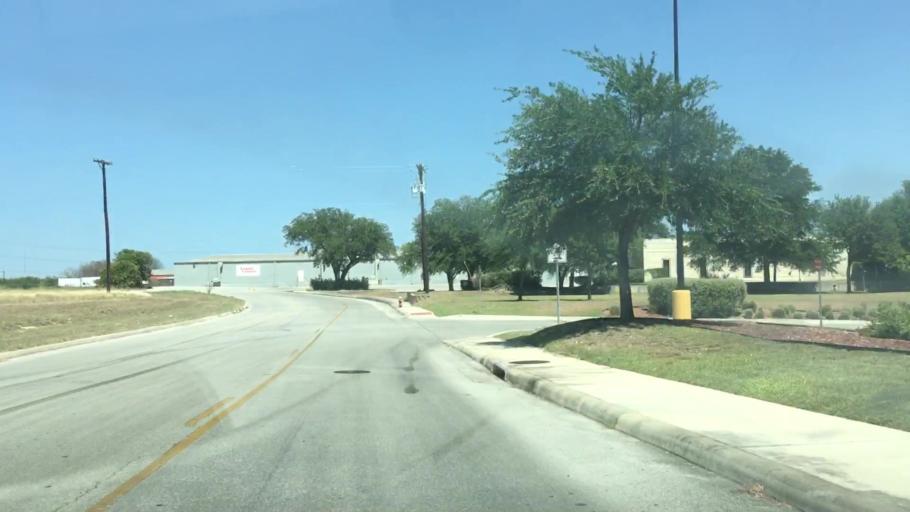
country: US
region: Texas
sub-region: Bexar County
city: Selma
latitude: 29.6052
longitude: -98.2753
